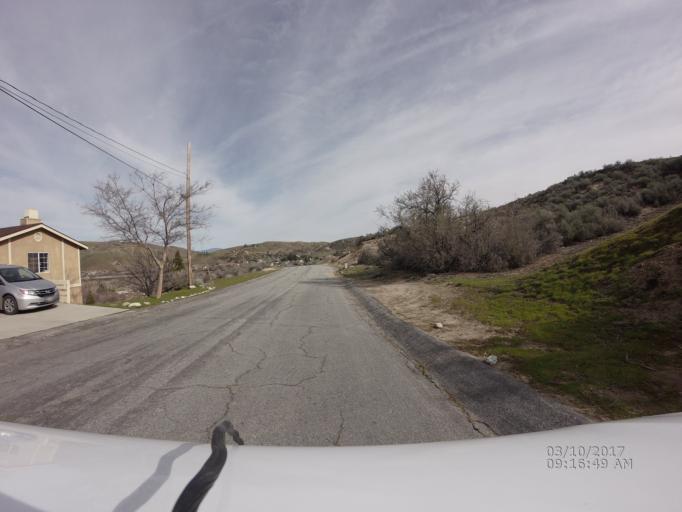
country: US
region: California
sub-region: Los Angeles County
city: Green Valley
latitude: 34.6591
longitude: -118.3909
